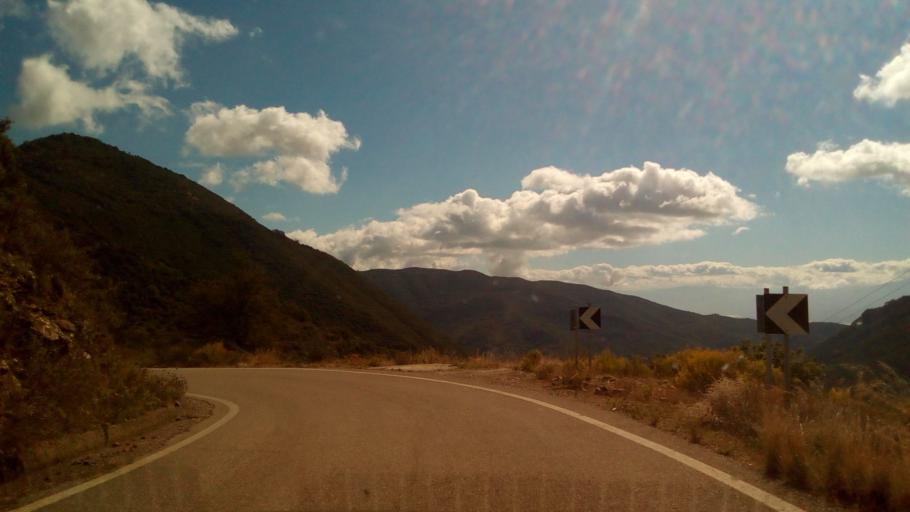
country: GR
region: West Greece
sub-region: Nomos Aitolias kai Akarnanias
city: Nafpaktos
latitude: 38.4821
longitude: 21.8588
